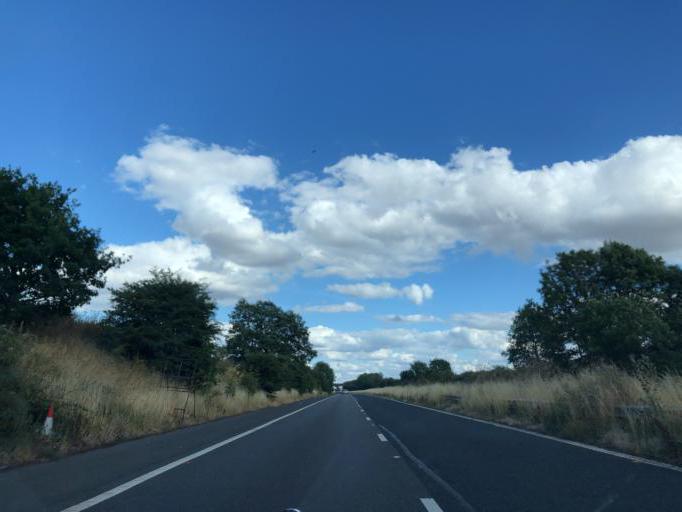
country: GB
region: England
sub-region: Northamptonshire
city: Daventry
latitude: 52.3293
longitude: -1.1713
